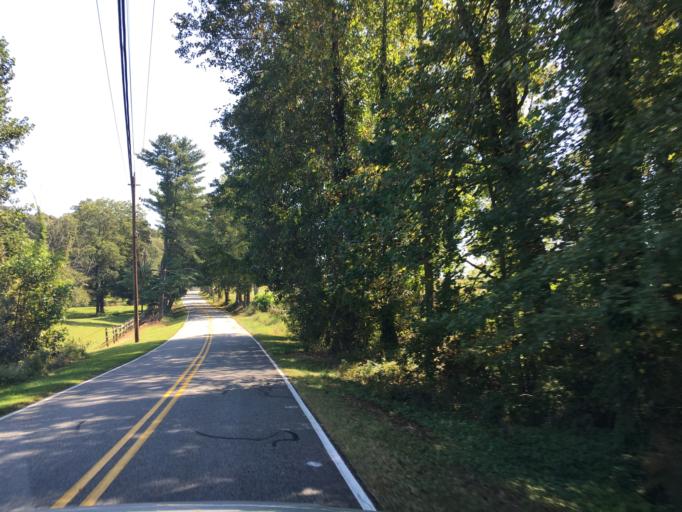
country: US
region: South Carolina
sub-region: Spartanburg County
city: Valley Falls
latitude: 35.0136
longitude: -81.9361
